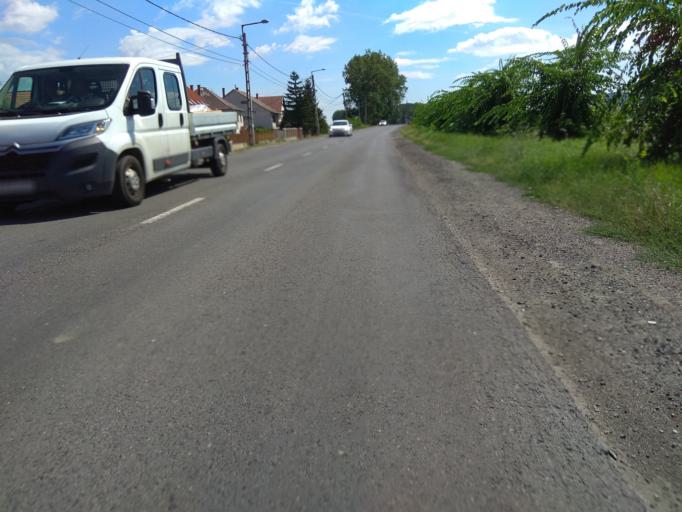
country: HU
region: Borsod-Abauj-Zemplen
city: Sajokaza
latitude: 48.2704
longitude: 20.5872
